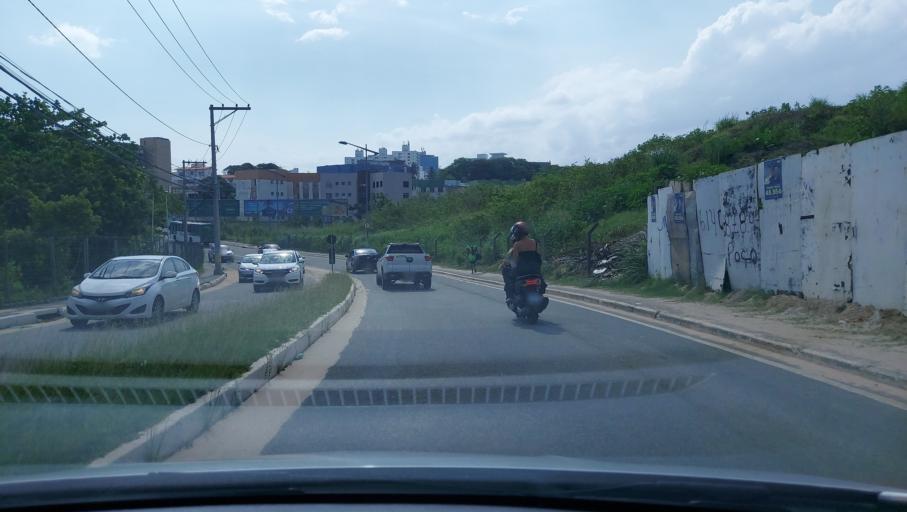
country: BR
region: Bahia
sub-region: Salvador
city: Salvador
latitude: -12.9812
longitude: -38.4418
